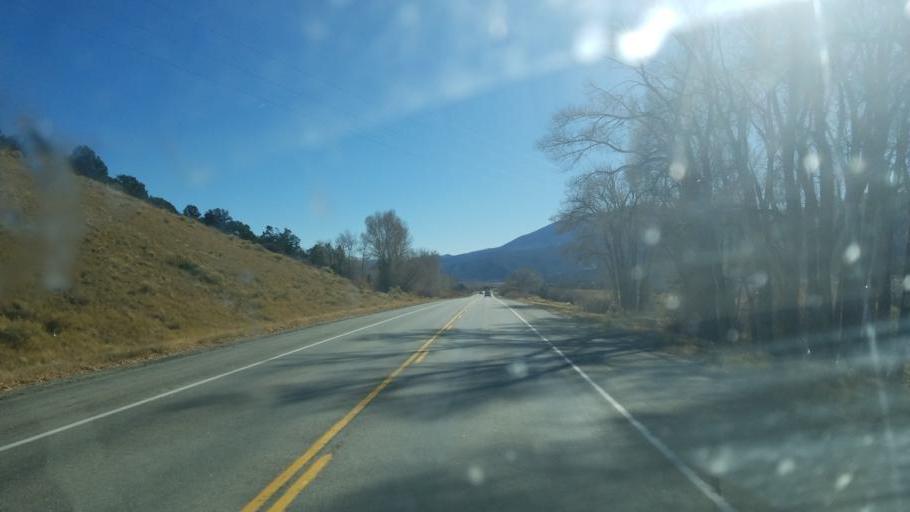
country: US
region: Colorado
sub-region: Chaffee County
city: Salida
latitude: 38.5308
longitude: -106.1375
